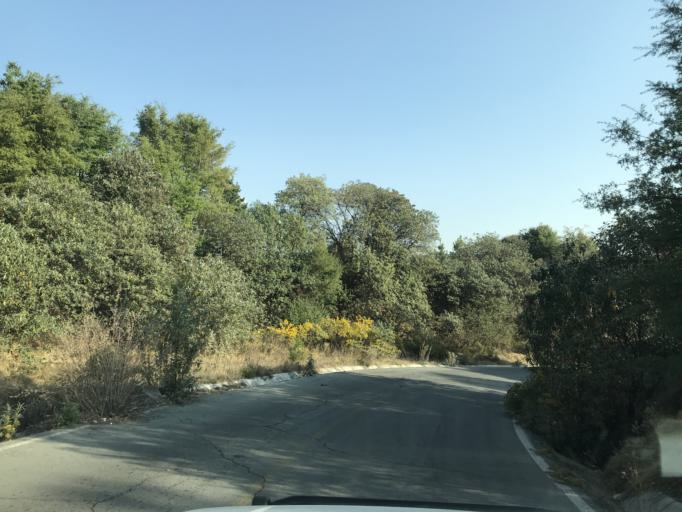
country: MX
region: Puebla
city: San Nicolas de los Ranchos
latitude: 19.0838
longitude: -98.5322
